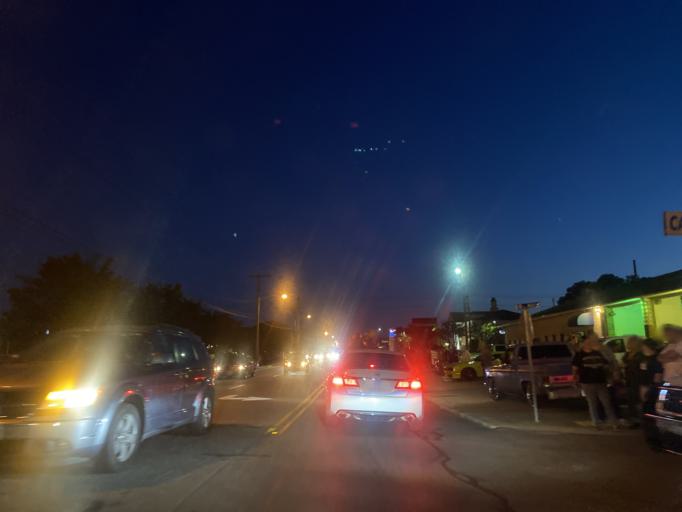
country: US
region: South Carolina
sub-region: Cherokee County
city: Gaffney
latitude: 35.0756
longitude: -81.6487
